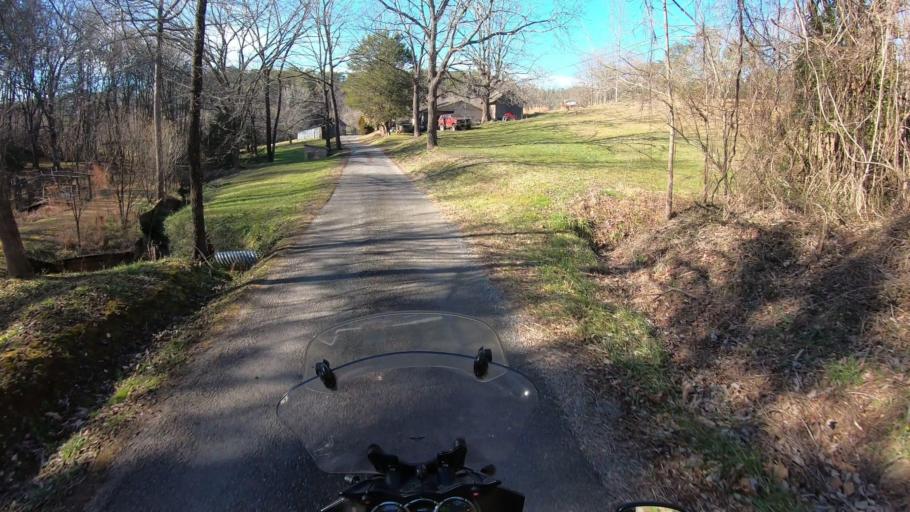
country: US
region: Georgia
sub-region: Fannin County
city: McCaysville
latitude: 34.9982
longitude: -84.3279
